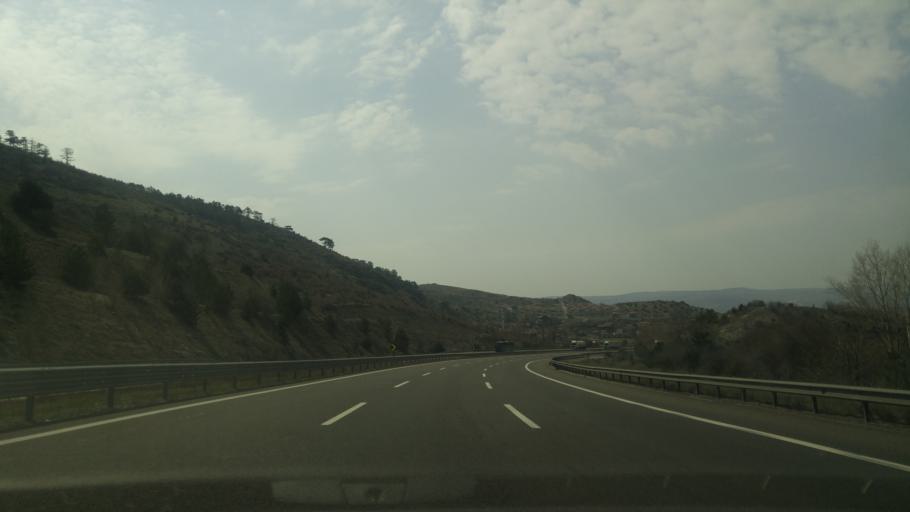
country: TR
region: Ankara
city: Celtikci
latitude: 40.3757
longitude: 32.4709
